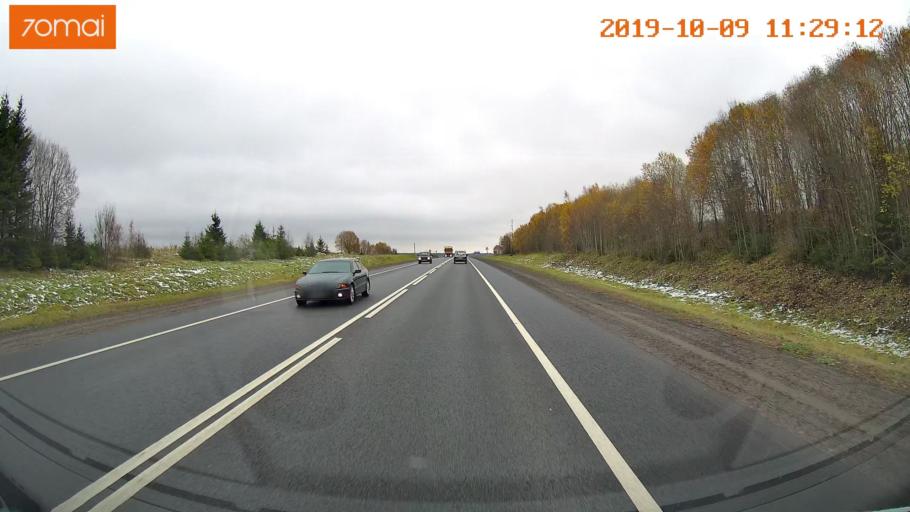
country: RU
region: Vologda
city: Vologda
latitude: 59.0638
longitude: 40.0496
